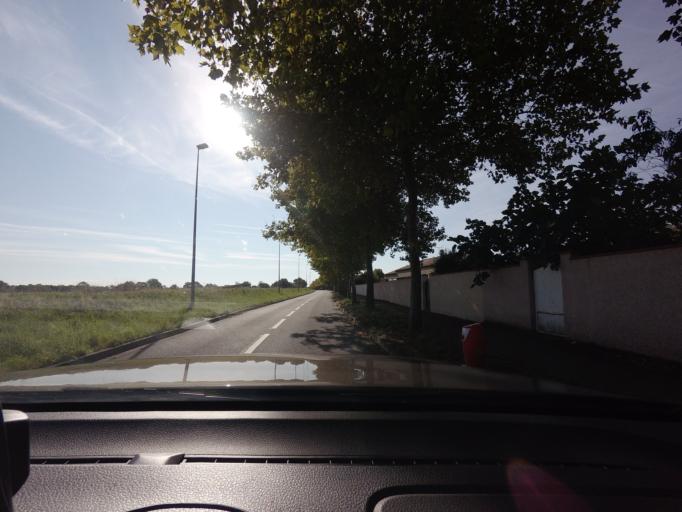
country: FR
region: Midi-Pyrenees
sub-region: Departement de la Haute-Garonne
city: Pibrac
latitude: 43.6225
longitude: 1.3069
